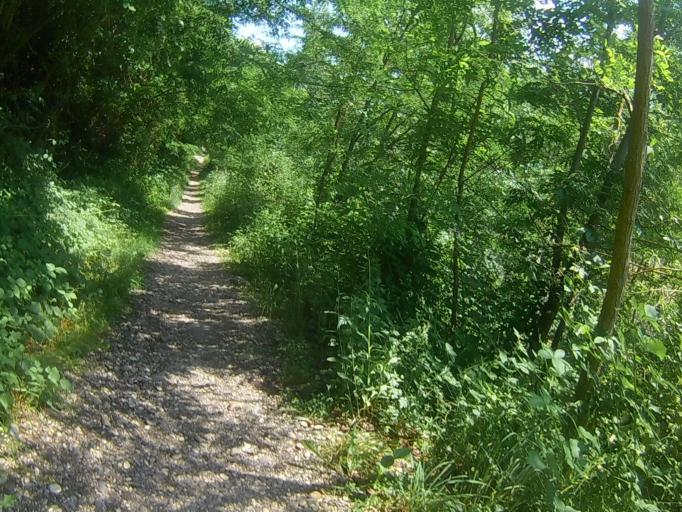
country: SI
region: Maribor
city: Kamnica
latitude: 46.5696
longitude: 15.6095
